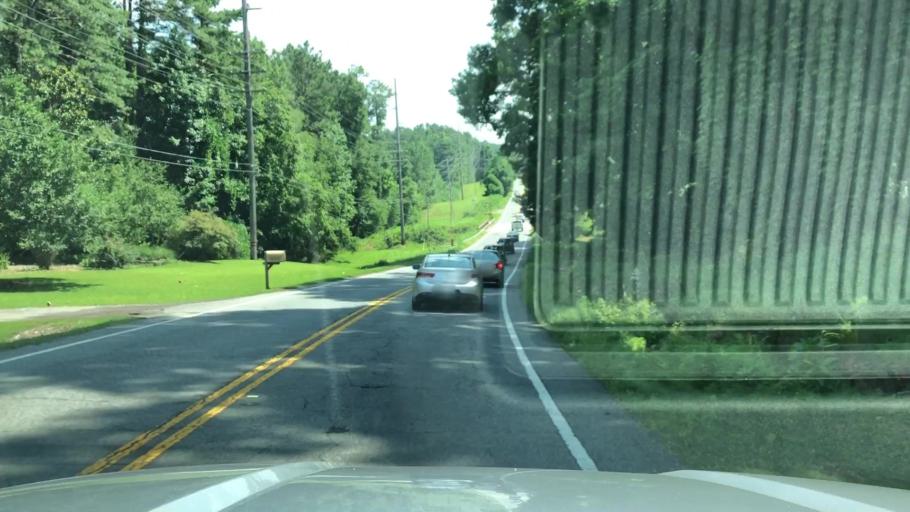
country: US
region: Georgia
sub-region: Cobb County
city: Acworth
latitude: 34.0177
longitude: -84.6991
